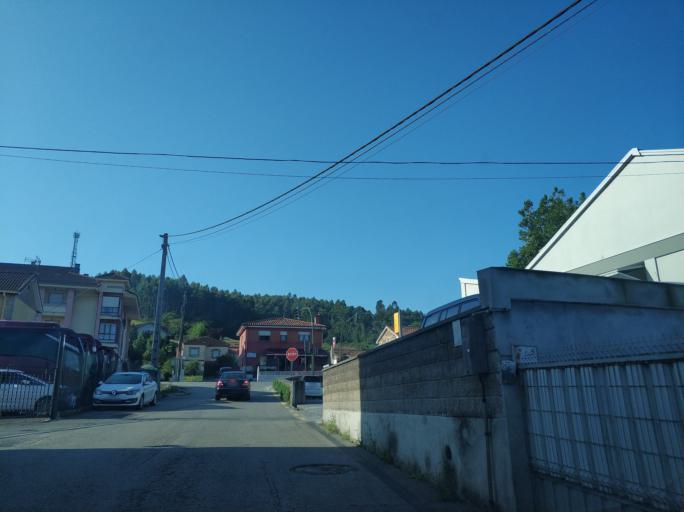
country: ES
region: Cantabria
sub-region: Provincia de Cantabria
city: Puente Viesgo
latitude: 43.3519
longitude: -3.9572
